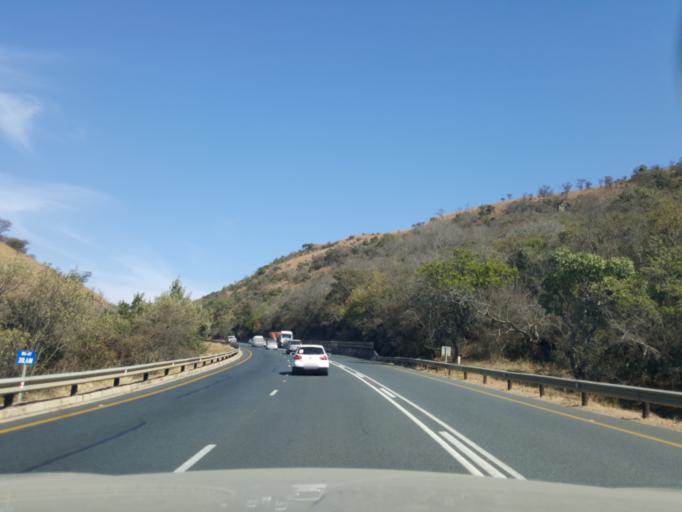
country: ZA
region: Mpumalanga
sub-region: Ehlanzeni District
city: Lydenburg
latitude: -25.4832
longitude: 30.3760
